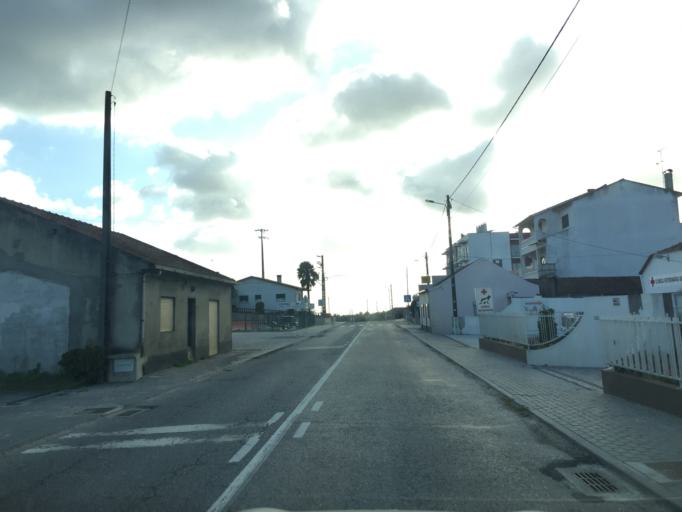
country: PT
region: Leiria
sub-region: Leiria
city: Monte Redondo
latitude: 39.9448
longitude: -8.7875
